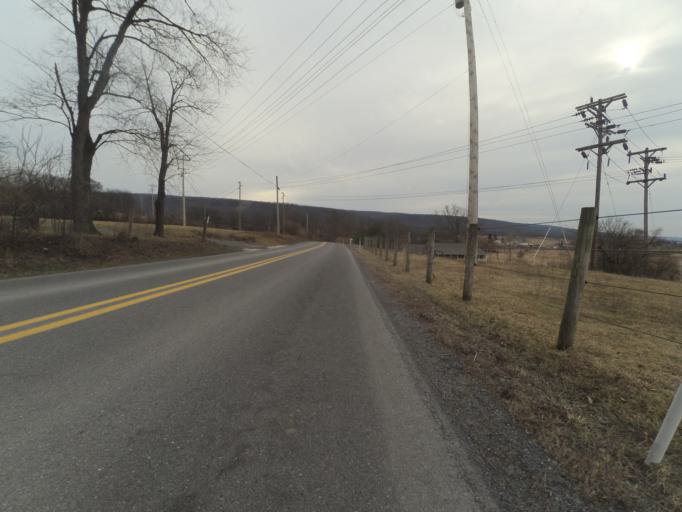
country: US
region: Pennsylvania
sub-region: Centre County
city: State College
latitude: 40.7648
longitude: -77.8415
